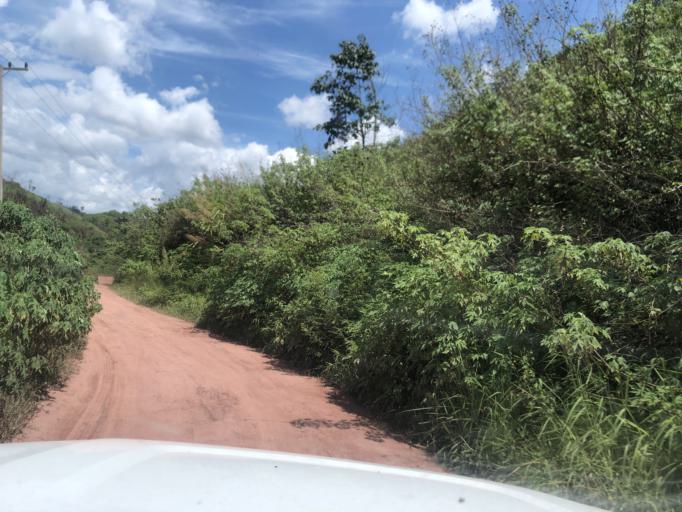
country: CN
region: Yunnan
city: Menglie
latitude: 22.2506
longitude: 101.6047
